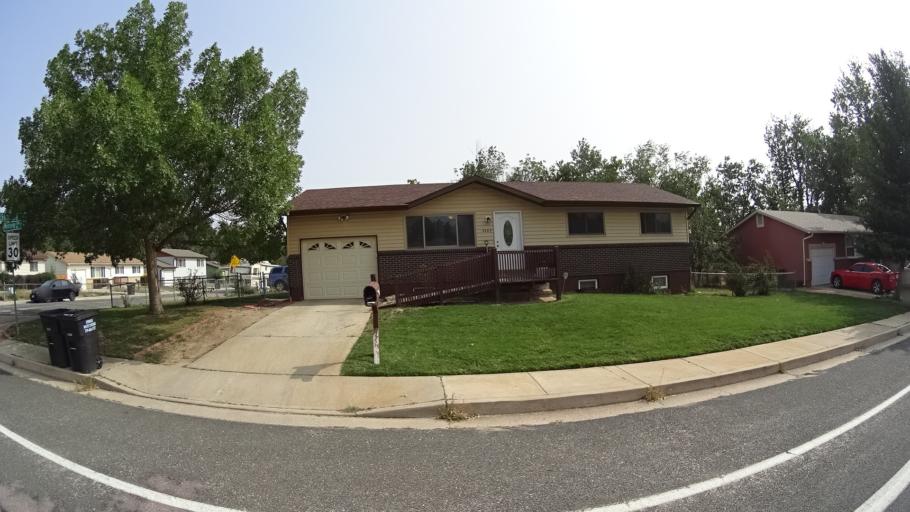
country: US
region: Colorado
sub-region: El Paso County
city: Stratmoor
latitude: 38.7973
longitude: -104.7669
